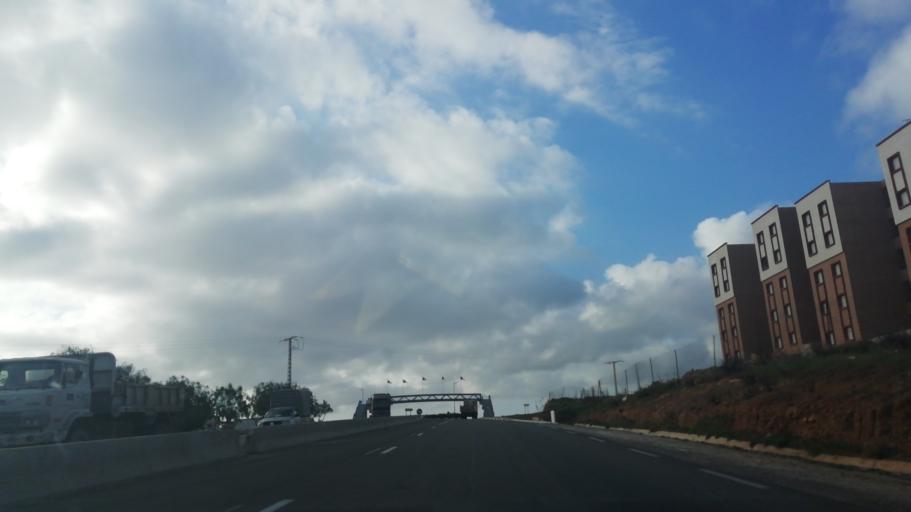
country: DZ
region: Mostaganem
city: Mostaganem
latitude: 36.1067
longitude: 0.2646
